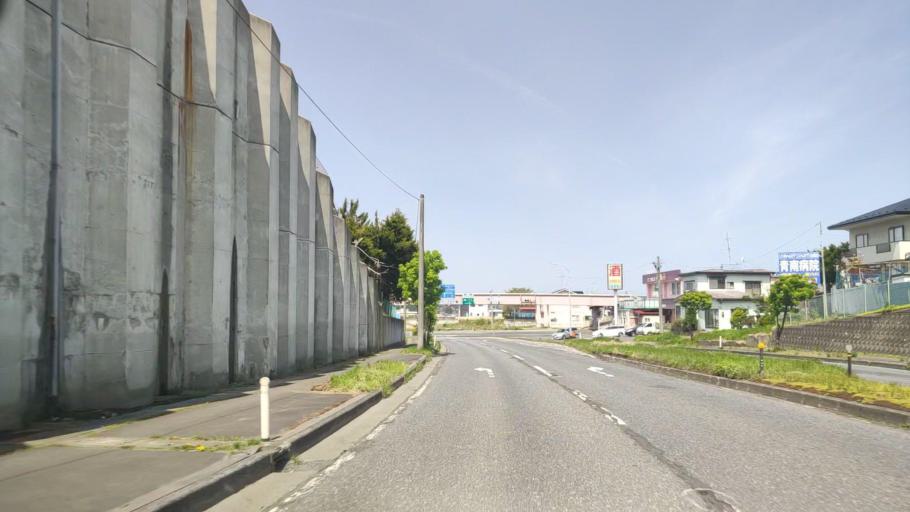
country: JP
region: Aomori
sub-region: Hachinohe Shi
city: Uchimaru
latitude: 40.5010
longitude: 141.4553
